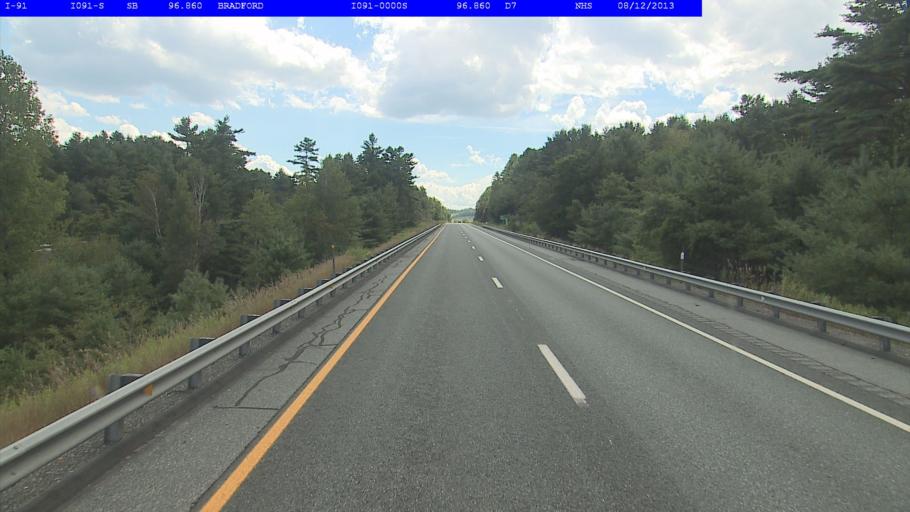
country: US
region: New Hampshire
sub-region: Grafton County
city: Orford
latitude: 43.9739
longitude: -72.1262
